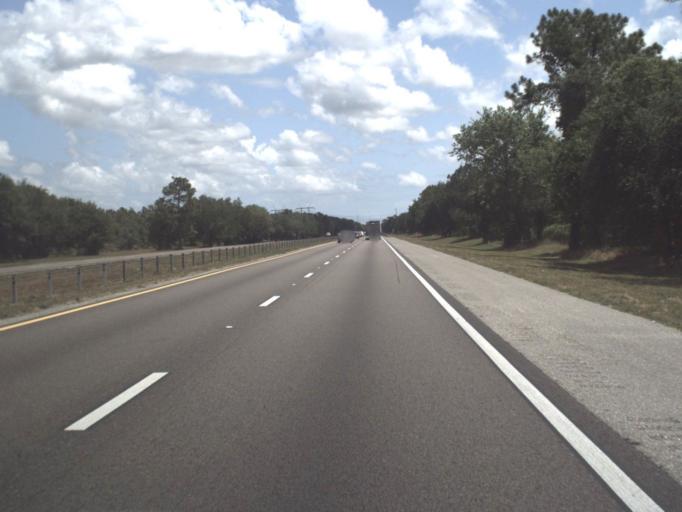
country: US
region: Florida
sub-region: Orange County
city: Wedgefield
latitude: 28.4523
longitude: -81.0229
